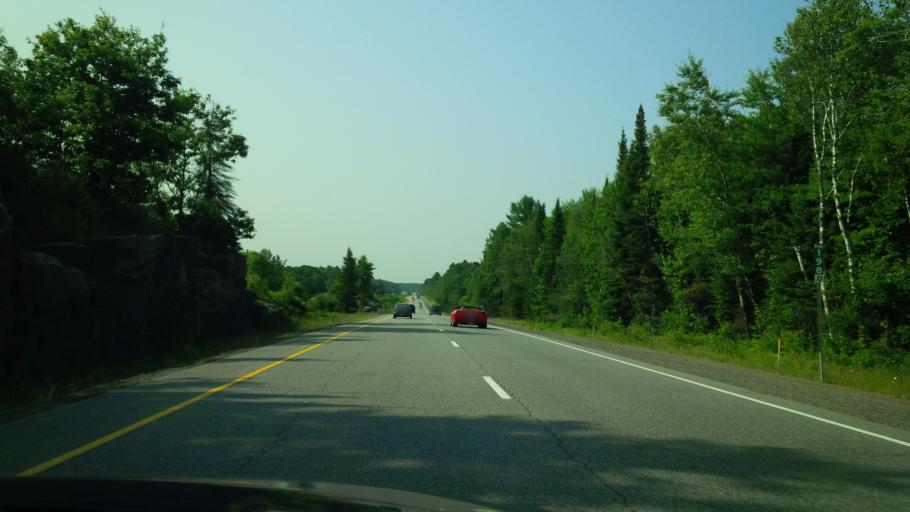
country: CA
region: Ontario
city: Bracebridge
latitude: 45.1344
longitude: -79.3113
